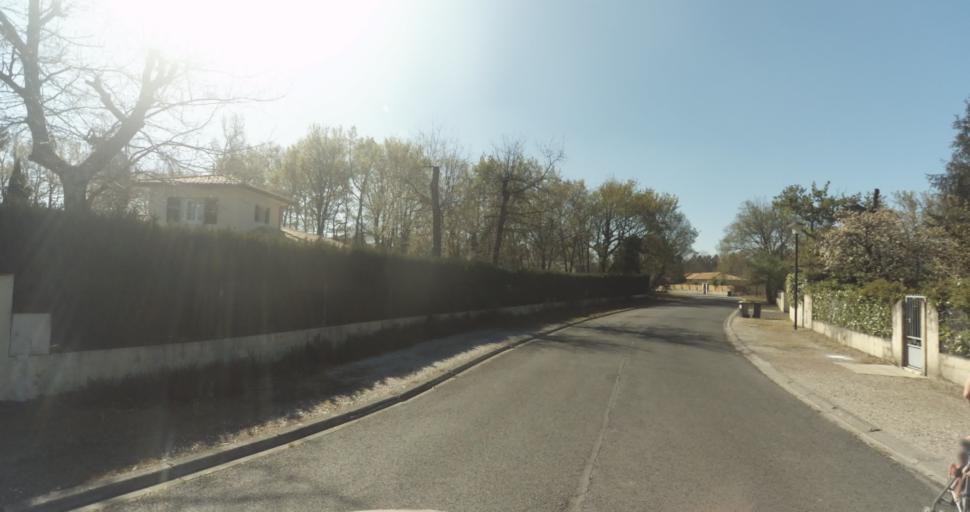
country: FR
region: Aquitaine
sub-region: Departement de la Gironde
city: Martignas-sur-Jalle
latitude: 44.7957
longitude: -0.8408
